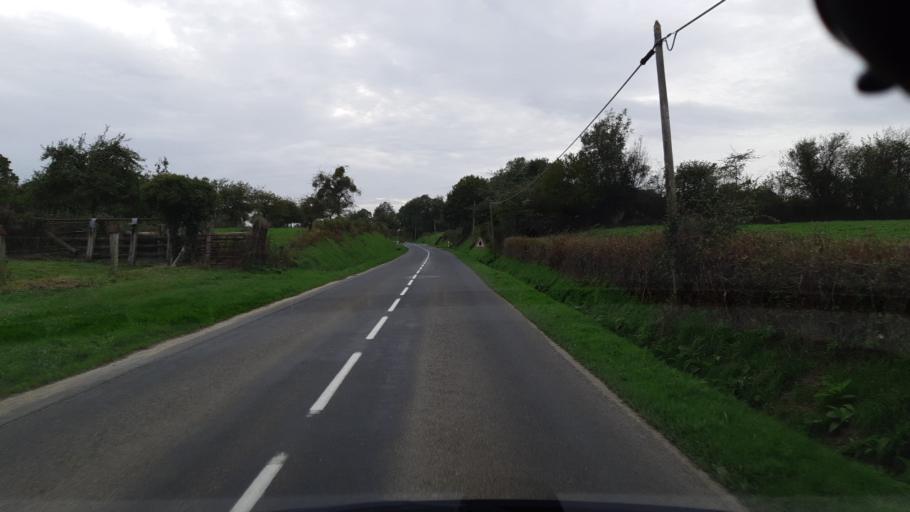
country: FR
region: Lower Normandy
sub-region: Departement de la Manche
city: Percy
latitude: 49.0015
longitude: -1.1905
